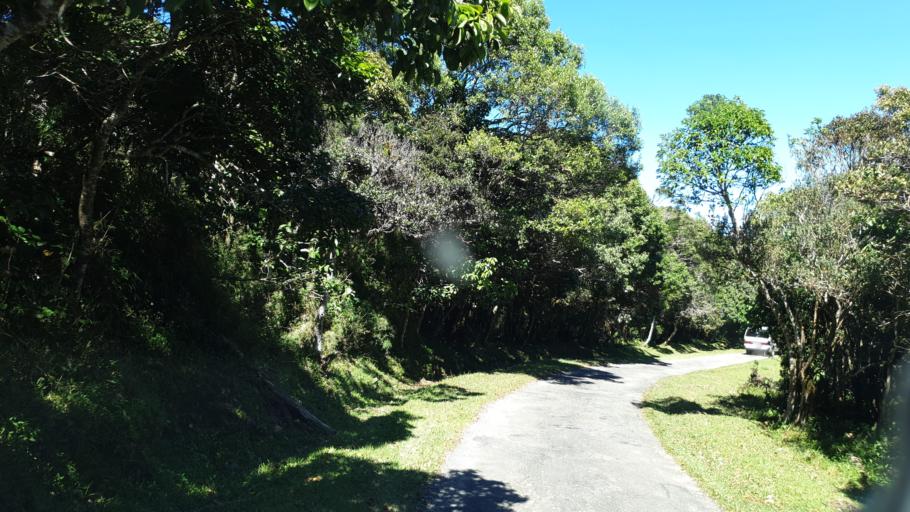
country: LK
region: Uva
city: Haputale
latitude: 6.8029
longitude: 80.8329
